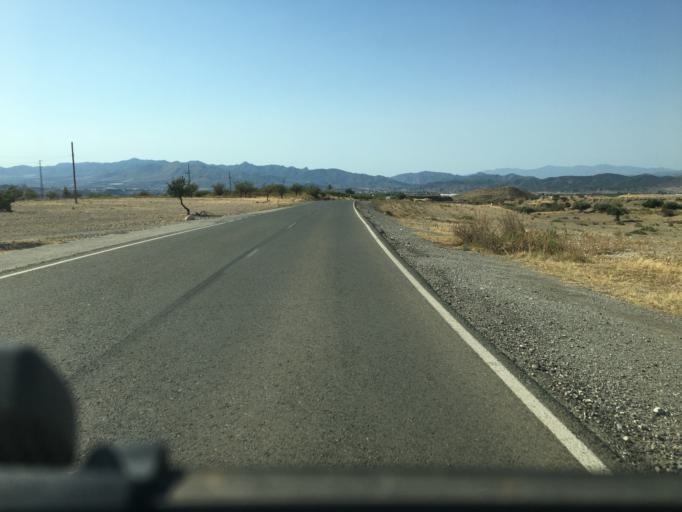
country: ES
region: Andalusia
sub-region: Provincia de Almeria
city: Huercal-Overa
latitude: 37.4384
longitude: -1.9763
